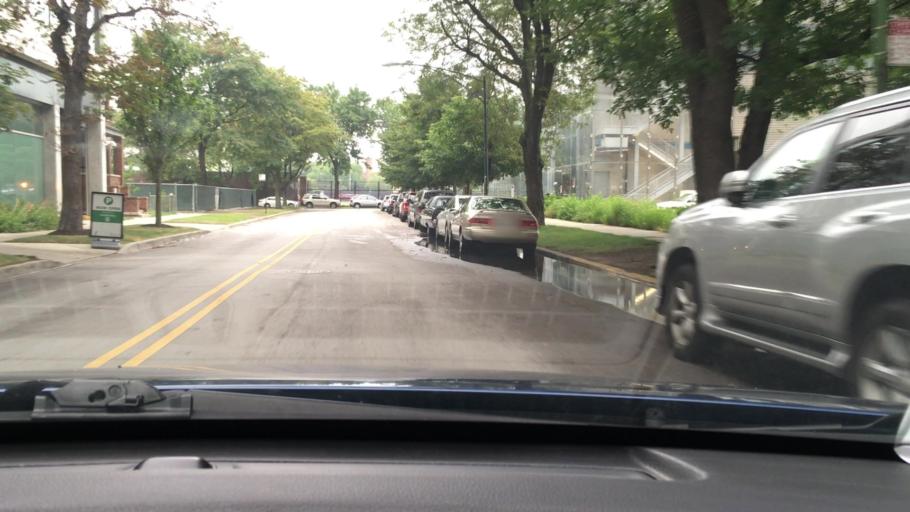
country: US
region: Illinois
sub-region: Cook County
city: Chicago
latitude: 41.7923
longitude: -87.6049
